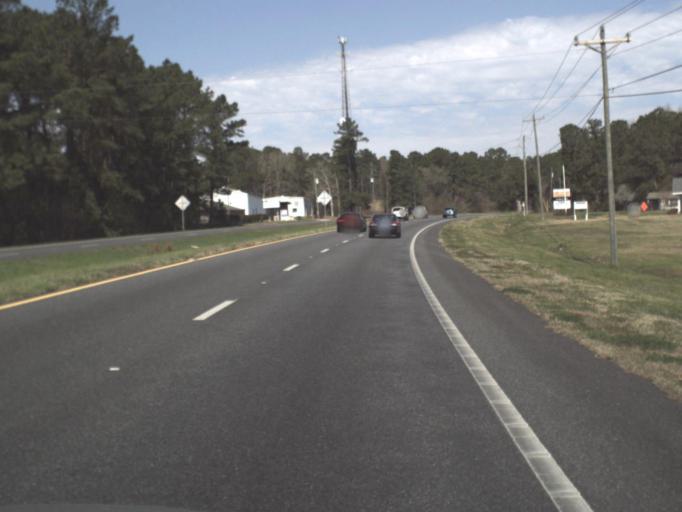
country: US
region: Florida
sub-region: Gadsden County
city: Havana
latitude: 30.6049
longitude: -84.4220
